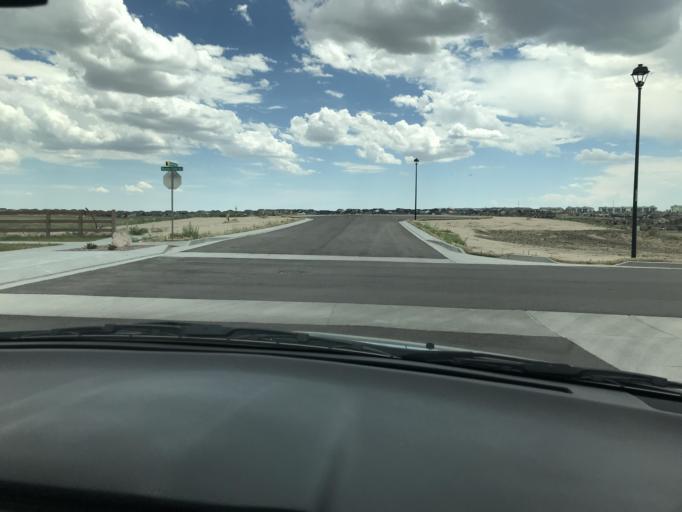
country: US
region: Colorado
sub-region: El Paso County
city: Black Forest
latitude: 38.9581
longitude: -104.7136
